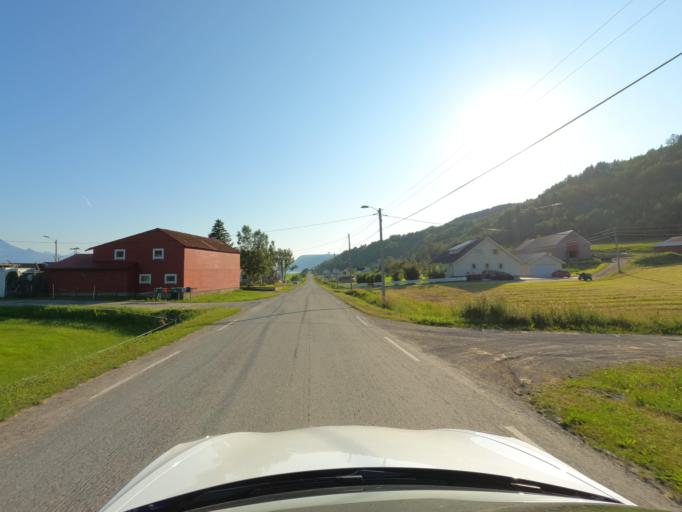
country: NO
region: Nordland
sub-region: Narvik
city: Bjerkvik
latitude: 68.5314
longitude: 17.4722
